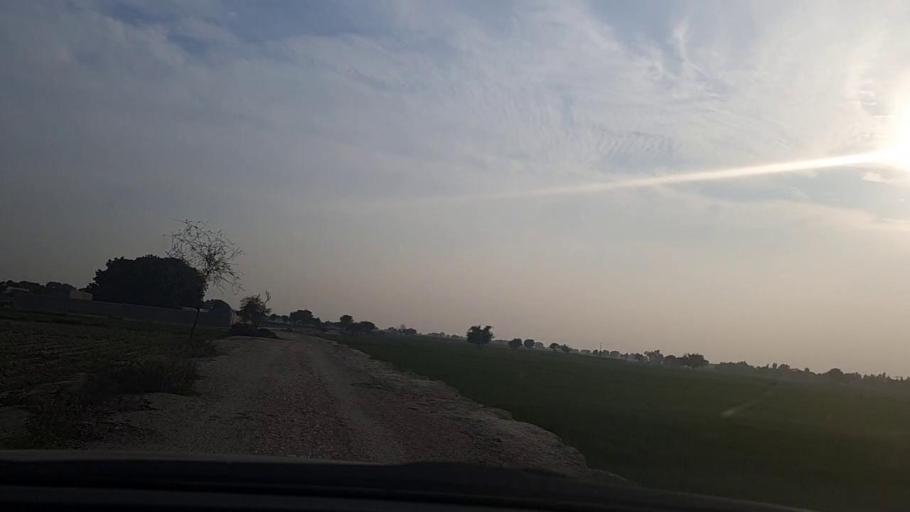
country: PK
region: Sindh
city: Daulatpur
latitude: 26.3358
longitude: 68.0236
